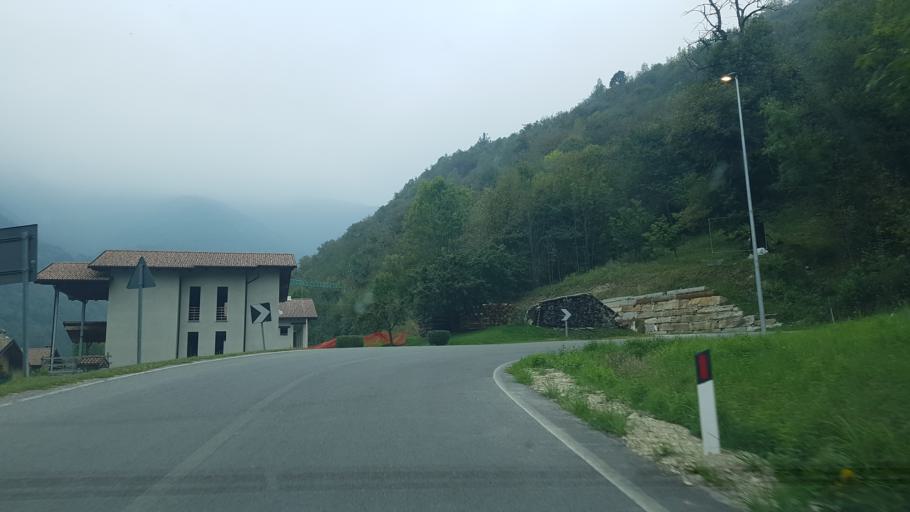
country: IT
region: Piedmont
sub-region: Provincia di Cuneo
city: Roccaforte Mondovi
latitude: 44.2750
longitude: 7.7386
